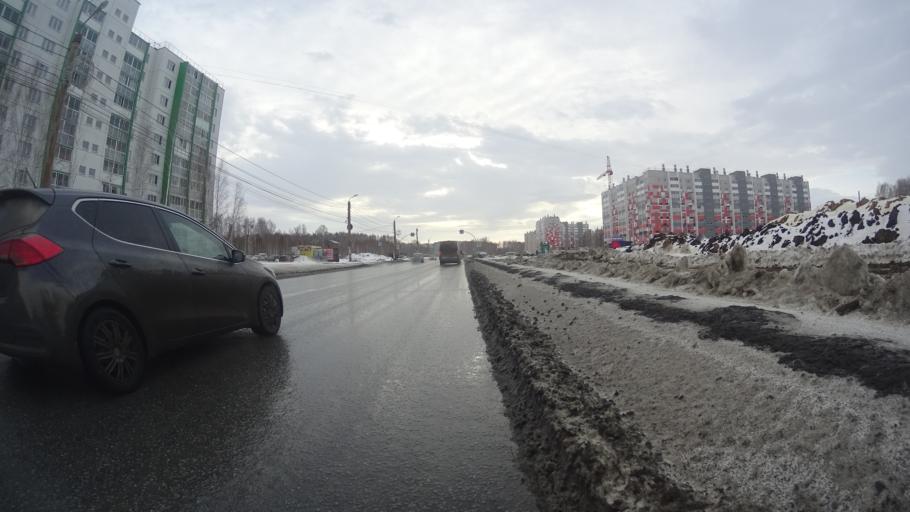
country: RU
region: Chelyabinsk
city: Roshchino
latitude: 55.2185
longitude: 61.2927
